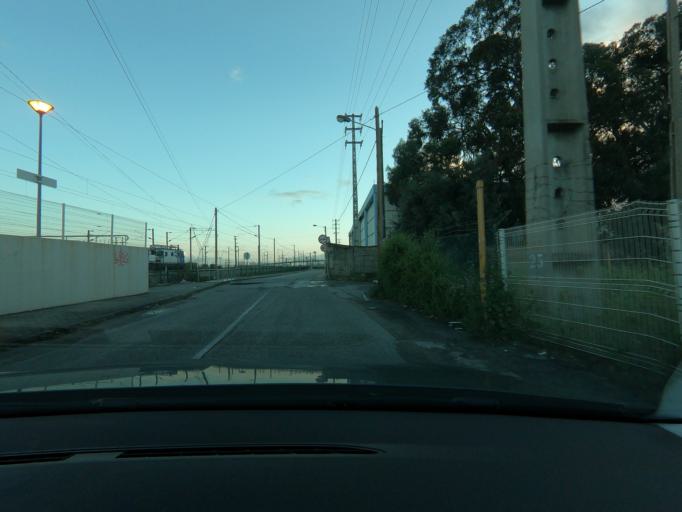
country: PT
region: Lisbon
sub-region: Vila Franca de Xira
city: Castanheira do Ribatejo
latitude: 38.9879
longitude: -8.9666
